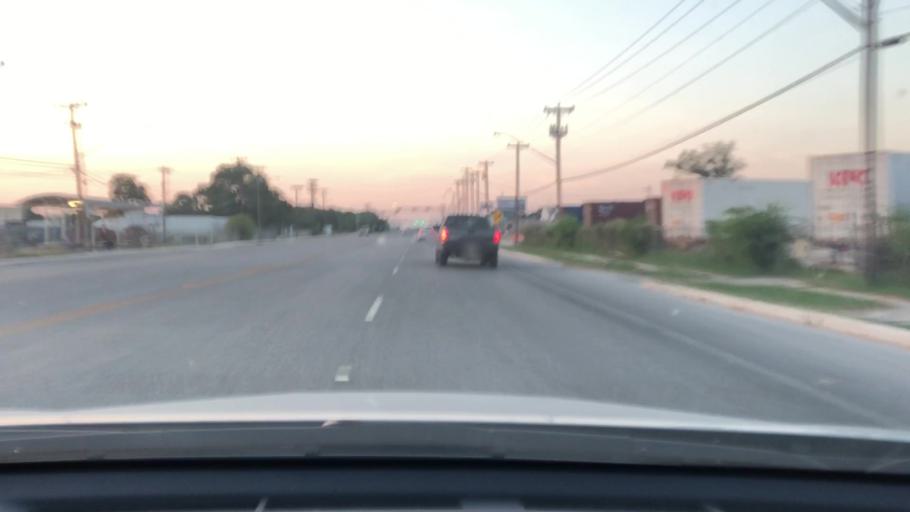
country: US
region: Texas
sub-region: Bexar County
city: Kirby
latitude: 29.4364
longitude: -98.4054
